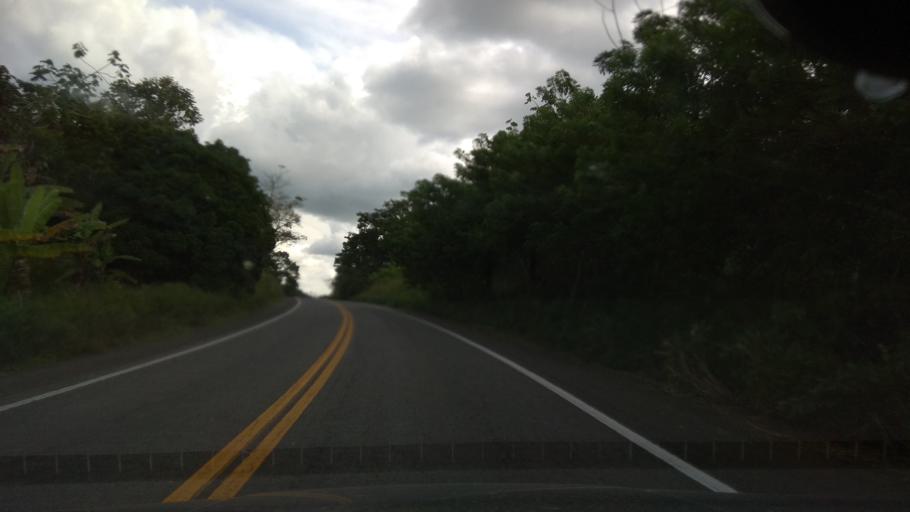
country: BR
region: Bahia
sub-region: Ubaitaba
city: Ubaitaba
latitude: -14.2619
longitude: -39.3355
